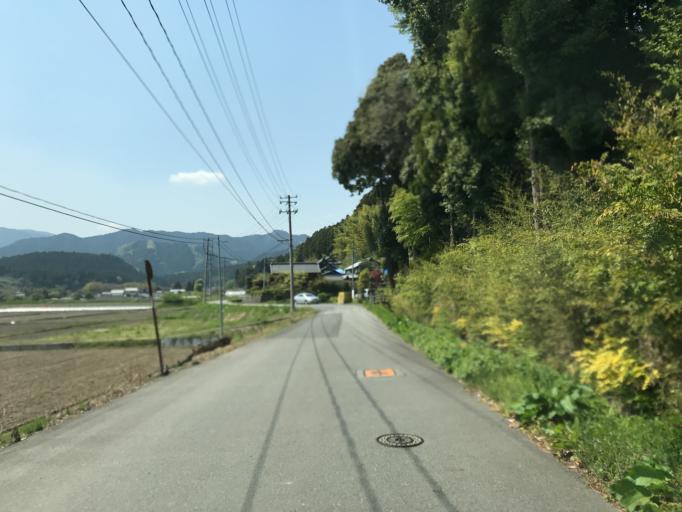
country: JP
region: Ibaraki
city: Kitaibaraki
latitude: 36.9277
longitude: 140.7493
